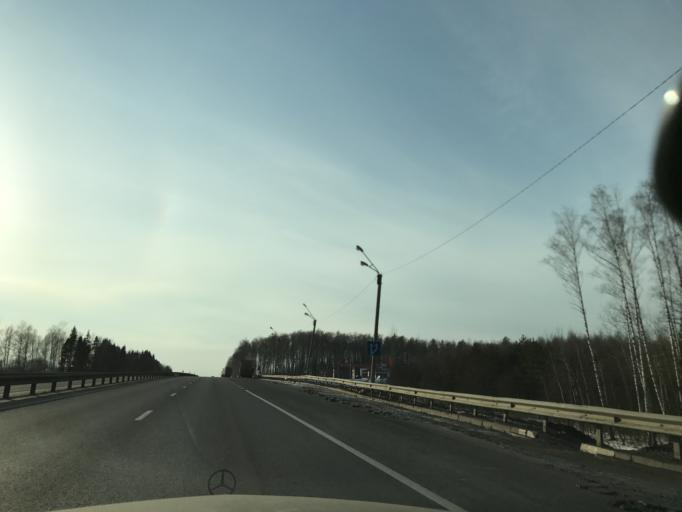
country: RU
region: Vladimir
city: Melekhovo
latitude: 56.2114
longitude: 41.3053
